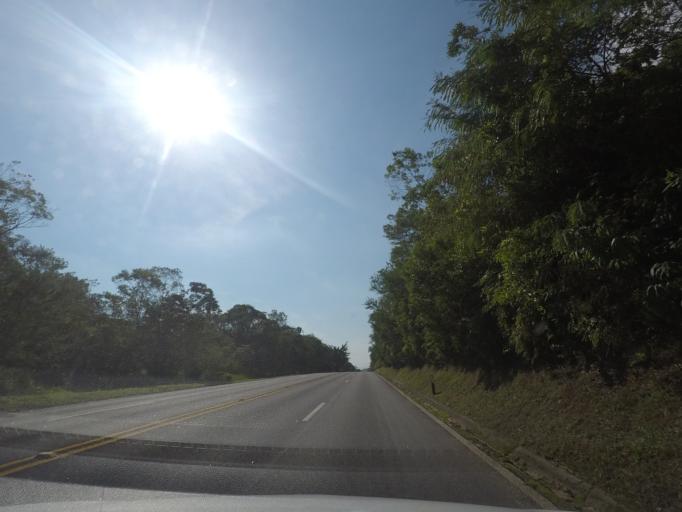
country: BR
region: Parana
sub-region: Paranagua
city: Paranagua
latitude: -25.5967
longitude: -48.6105
